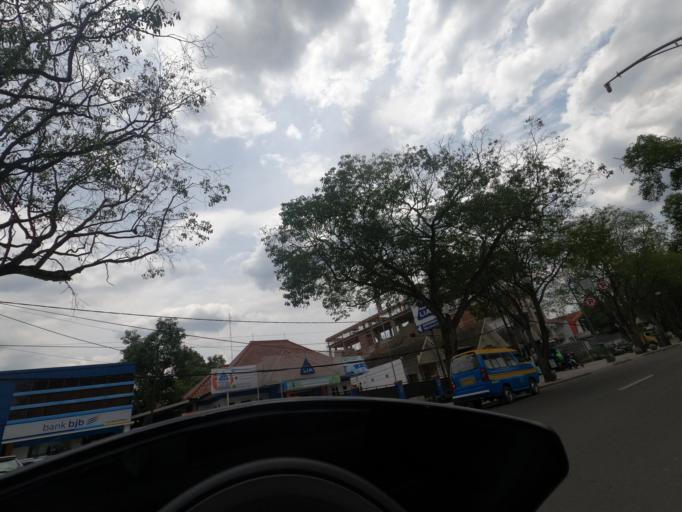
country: ID
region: West Java
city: Bandung
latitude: -6.9093
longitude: 107.6254
